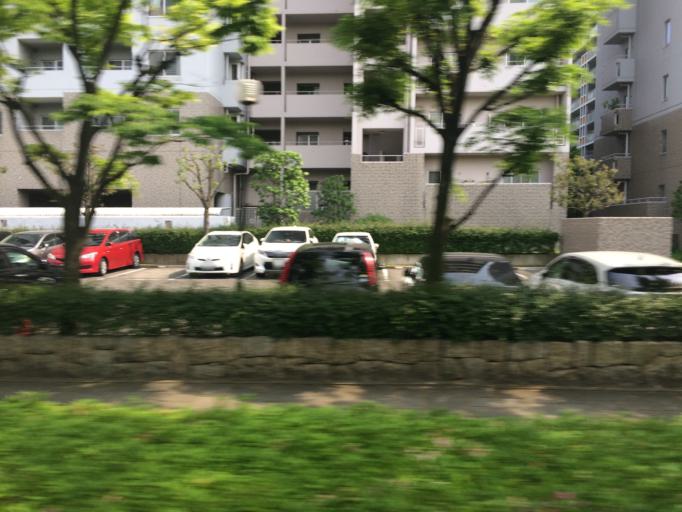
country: JP
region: Hyogo
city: Ashiya
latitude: 34.6928
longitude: 135.2717
